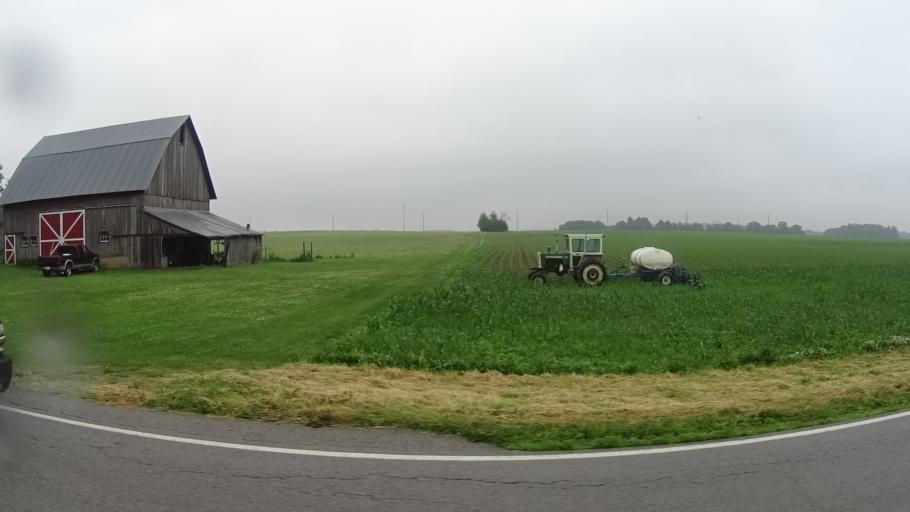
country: US
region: Ohio
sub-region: Huron County
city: Bellevue
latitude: 41.3356
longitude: -82.8434
